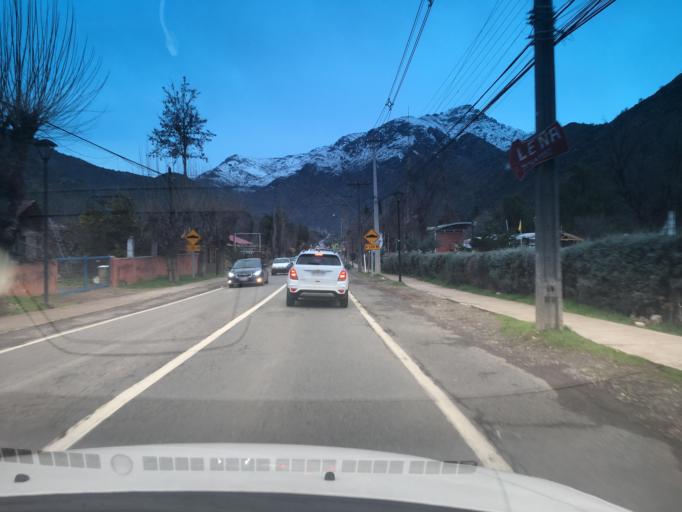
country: CL
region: Santiago Metropolitan
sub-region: Provincia de Cordillera
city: Puente Alto
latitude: -33.6928
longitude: -70.3354
